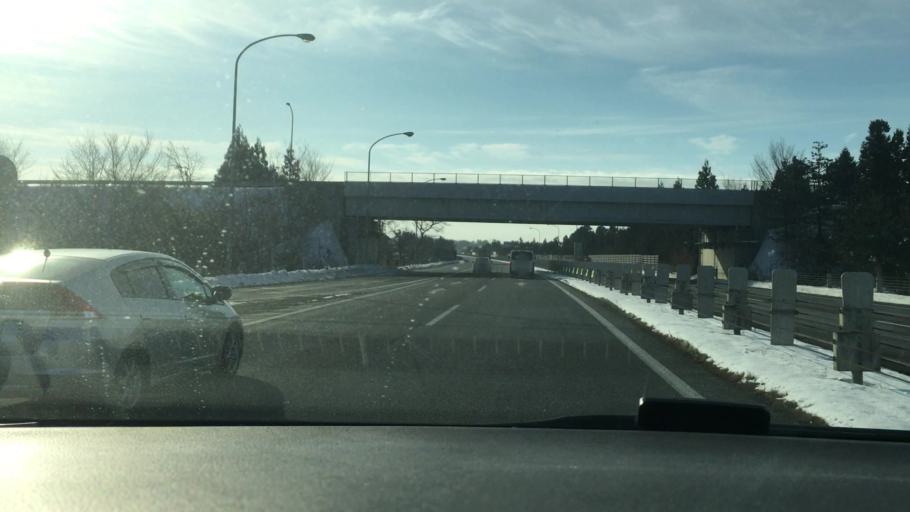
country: JP
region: Iwate
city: Hanamaki
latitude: 39.3868
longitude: 141.0915
